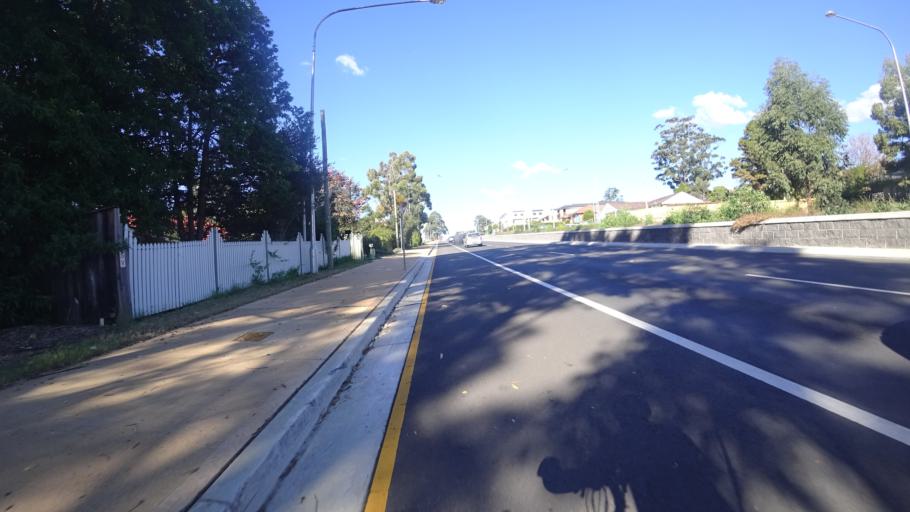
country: AU
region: New South Wales
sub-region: The Hills Shire
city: Castle Hill
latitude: -33.7308
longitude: 150.9988
